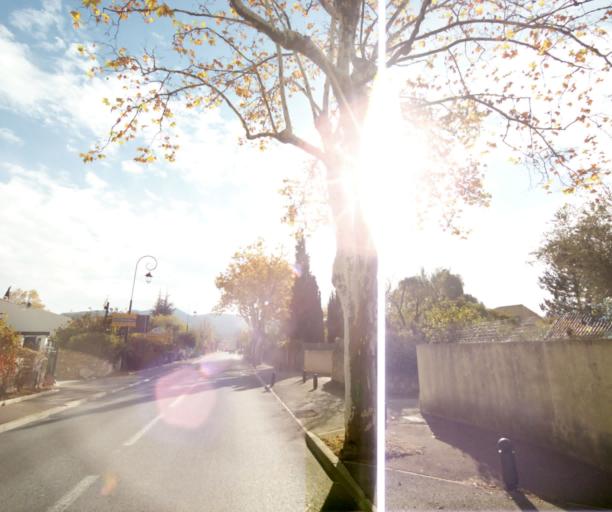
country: FR
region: Provence-Alpes-Cote d'Azur
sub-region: Departement des Bouches-du-Rhone
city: Gemenos
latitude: 43.2988
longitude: 5.6215
